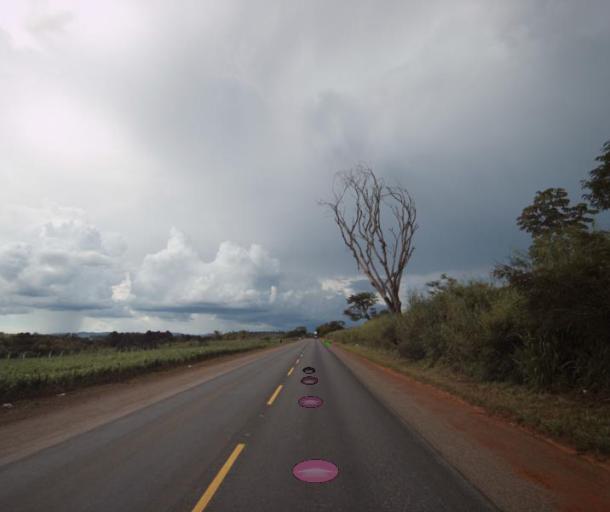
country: BR
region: Goias
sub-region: Ceres
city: Ceres
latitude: -15.2107
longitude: -49.5474
